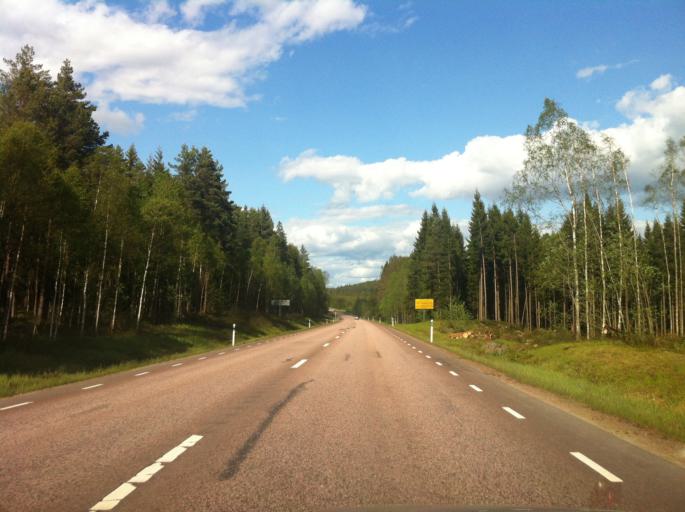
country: SE
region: Vaermland
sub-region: Kristinehamns Kommun
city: Kristinehamn
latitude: 59.3605
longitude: 14.1524
